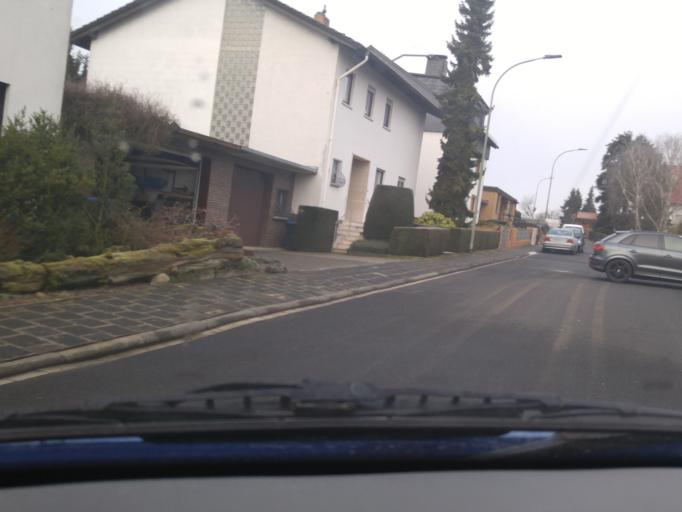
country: DE
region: Hesse
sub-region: Regierungsbezirk Darmstadt
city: Karben
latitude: 50.2560
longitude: 8.7523
